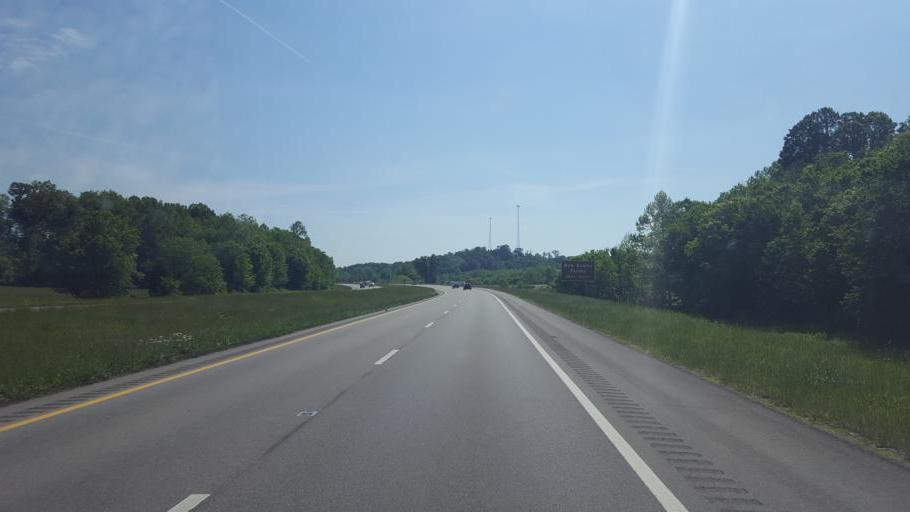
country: US
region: Ohio
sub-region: Jackson County
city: Oak Hill
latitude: 38.8874
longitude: -82.3938
